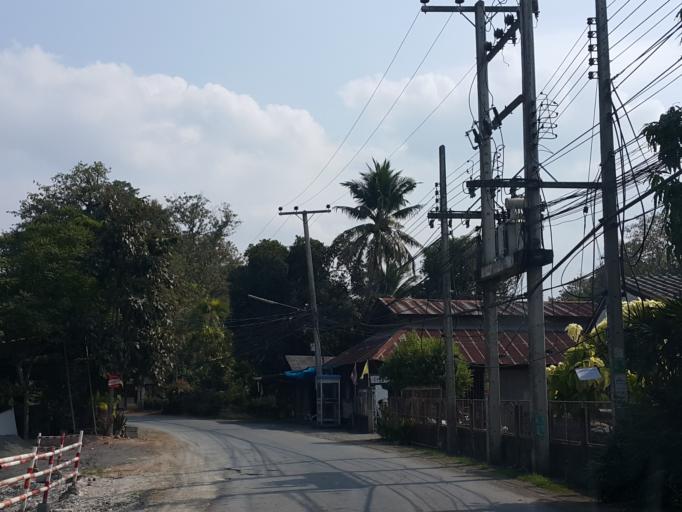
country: TH
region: Chiang Mai
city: Mae On
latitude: 18.8210
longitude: 99.1743
